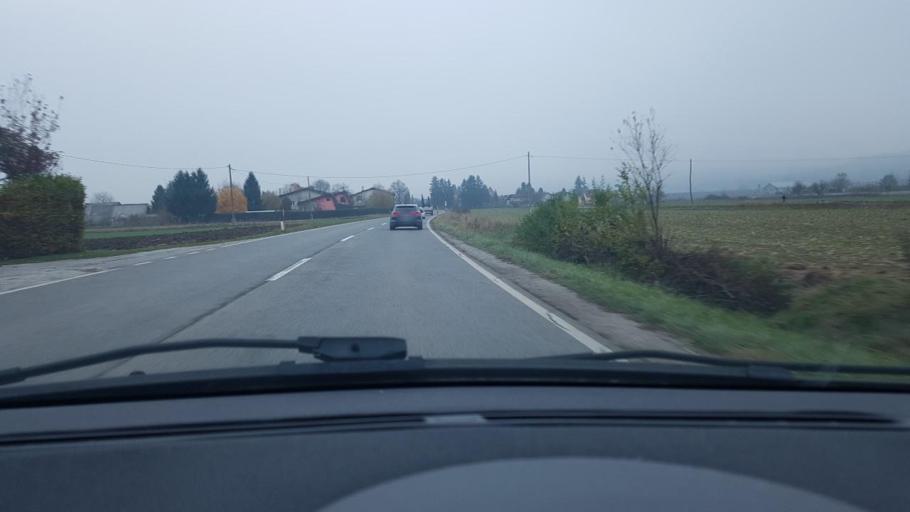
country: SI
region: Zalec
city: Zalec
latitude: 46.2467
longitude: 15.1941
